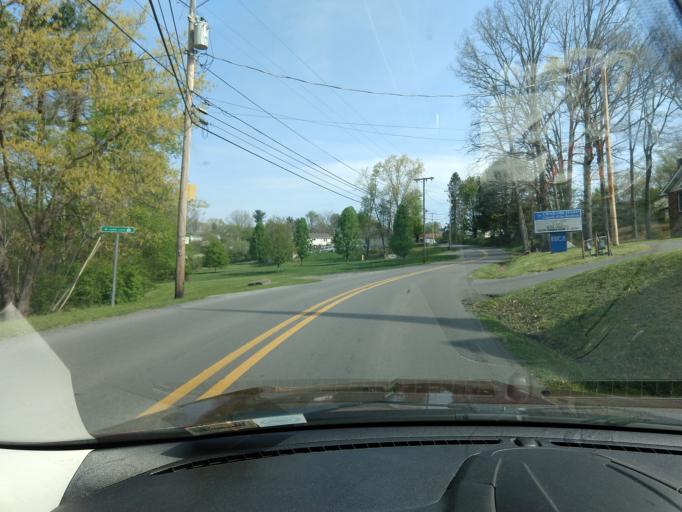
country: US
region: West Virginia
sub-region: Raleigh County
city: Crab Orchard
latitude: 37.7435
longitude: -81.2312
